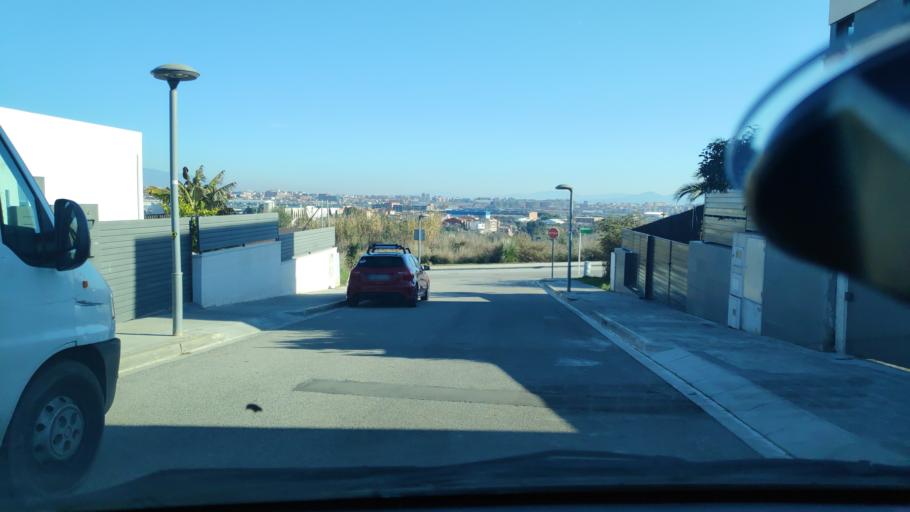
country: ES
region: Catalonia
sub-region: Provincia de Barcelona
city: Sant Quirze del Valles
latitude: 41.5251
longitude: 2.0825
